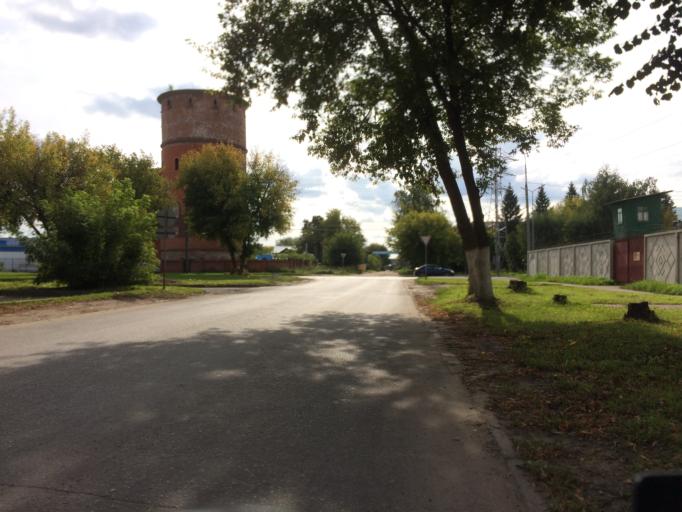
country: RU
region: Mariy-El
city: Yoshkar-Ola
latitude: 56.6307
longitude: 47.8736
